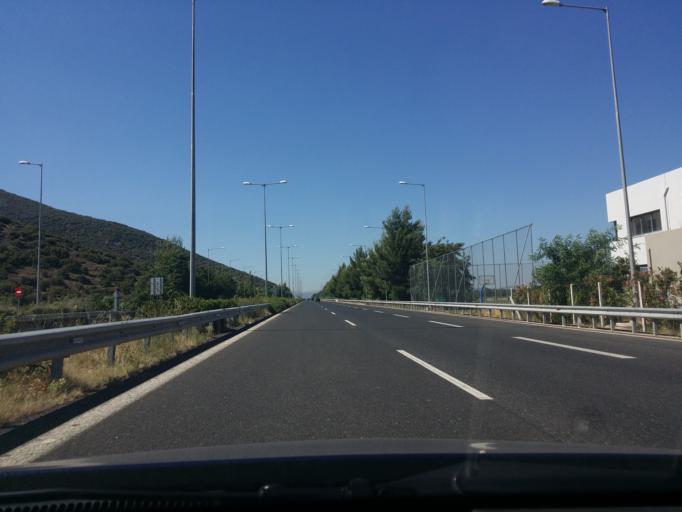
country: GR
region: Peloponnese
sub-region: Nomos Arkadias
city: Tripoli
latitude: 37.5795
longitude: 22.4312
